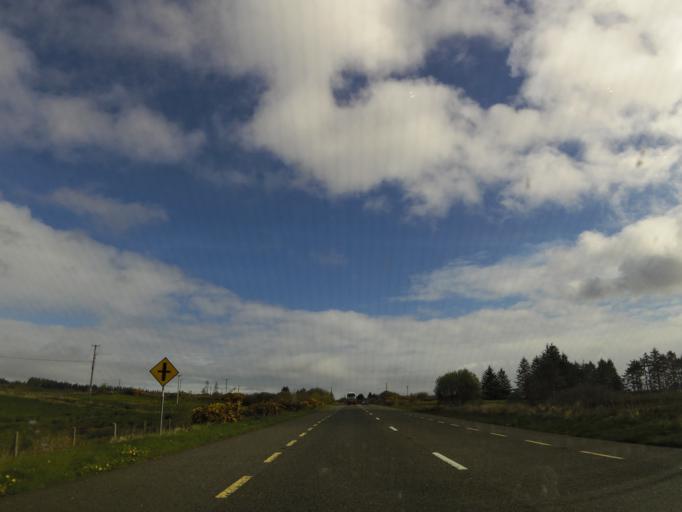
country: IE
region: Connaught
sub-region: Maigh Eo
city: Ballyhaunis
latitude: 53.9025
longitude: -8.7974
